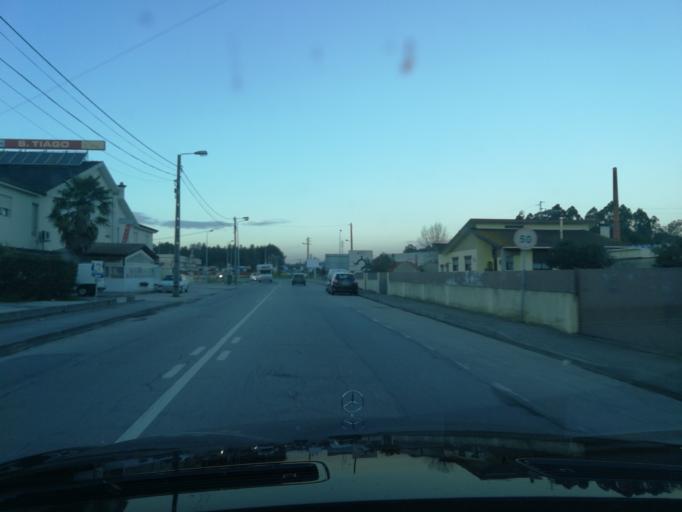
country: PT
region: Aveiro
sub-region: Estarreja
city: Beduido
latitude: 40.7685
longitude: -8.5708
